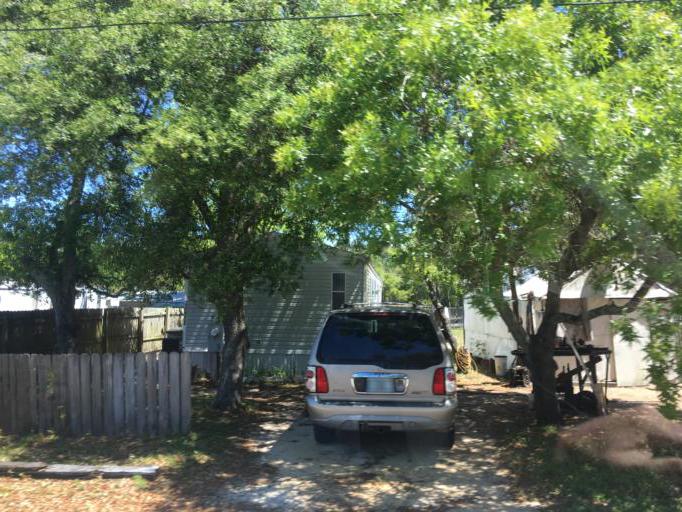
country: US
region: Florida
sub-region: Bay County
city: Laguna Beach
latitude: 30.2546
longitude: -85.9381
